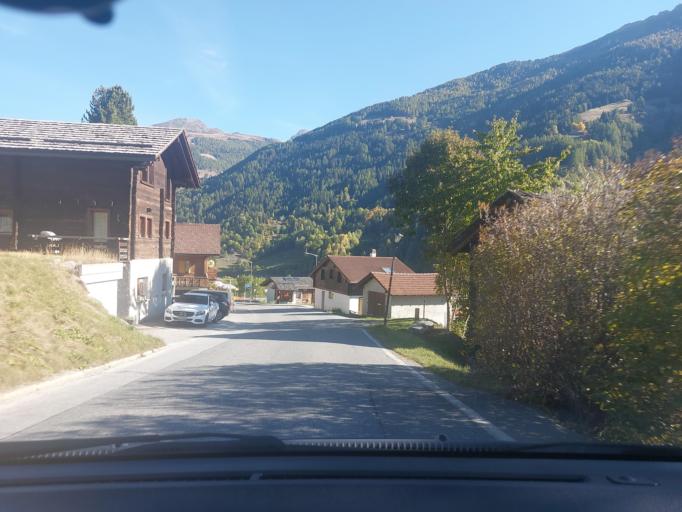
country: CH
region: Valais
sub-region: Sierre District
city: Chippis
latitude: 46.1971
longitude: 7.5857
